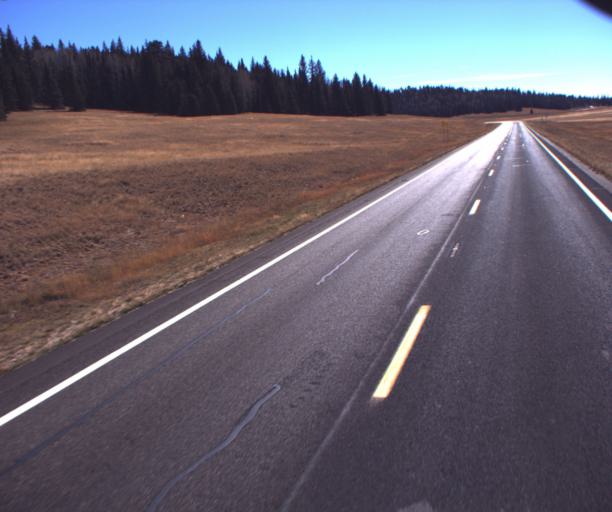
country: US
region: Arizona
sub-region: Coconino County
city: Grand Canyon
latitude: 36.4283
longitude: -112.1320
